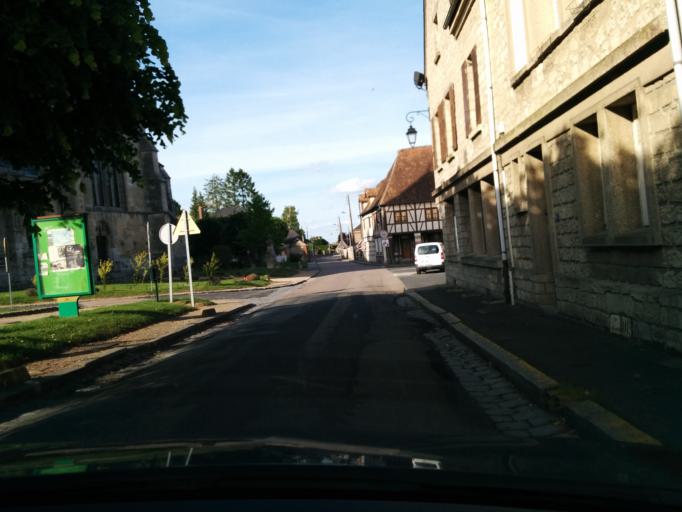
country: FR
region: Haute-Normandie
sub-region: Departement de l'Eure
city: Les Andelys
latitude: 49.3103
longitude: 1.4324
